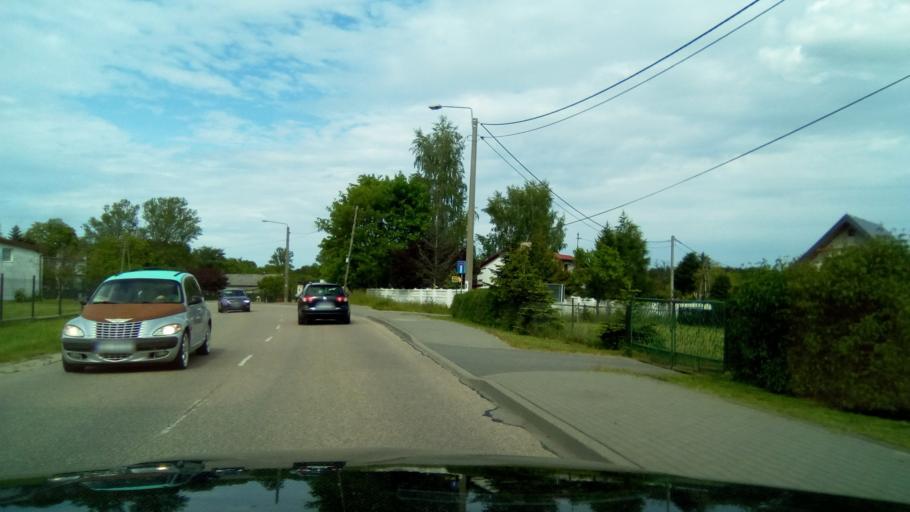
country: PL
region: Pomeranian Voivodeship
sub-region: Powiat pucki
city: Wierzchucino
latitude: 54.7802
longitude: 17.9656
